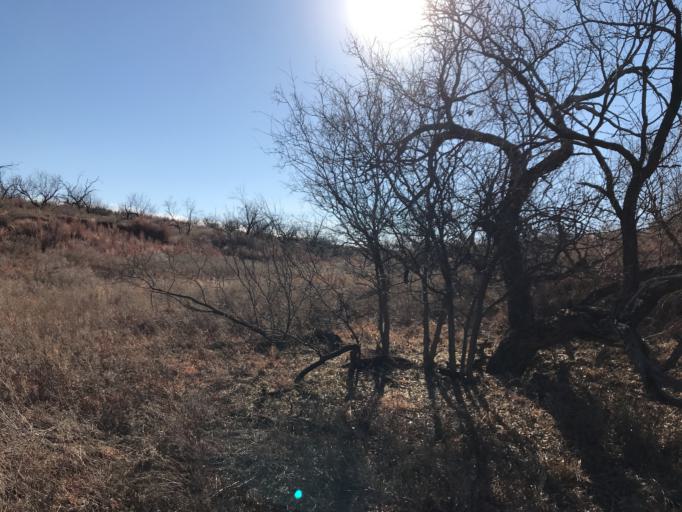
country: US
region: Texas
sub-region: Childress County
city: Childress
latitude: 34.3251
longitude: -100.4745
